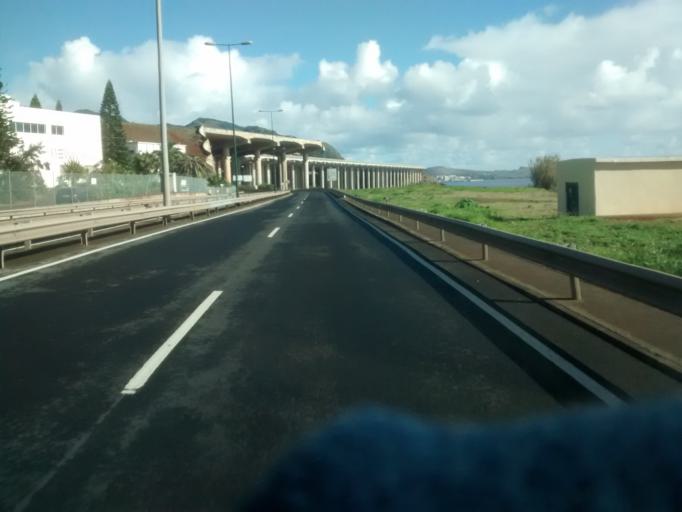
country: PT
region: Madeira
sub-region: Machico
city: Machico
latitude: 32.6960
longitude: -16.7721
